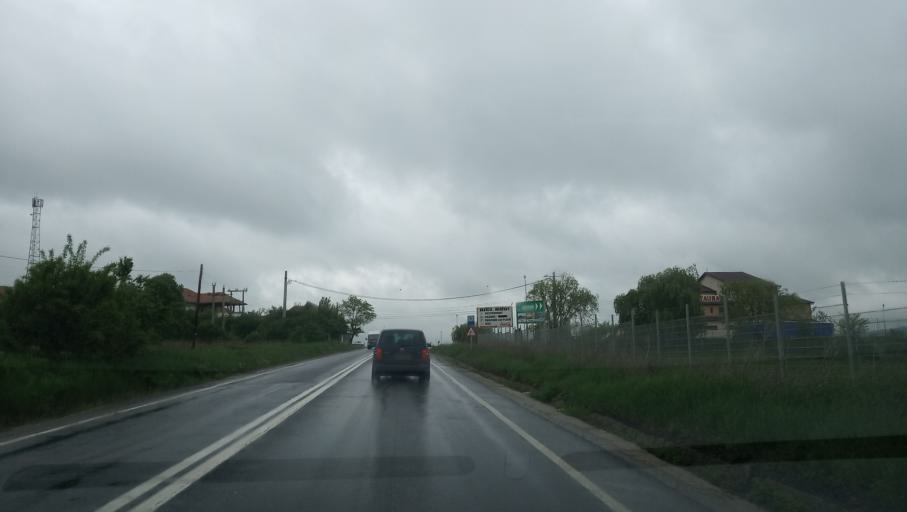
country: RO
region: Sibiu
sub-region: Oras Miercurea Sibiului
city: Miercurea Sibiului
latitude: 45.8786
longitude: 23.7996
